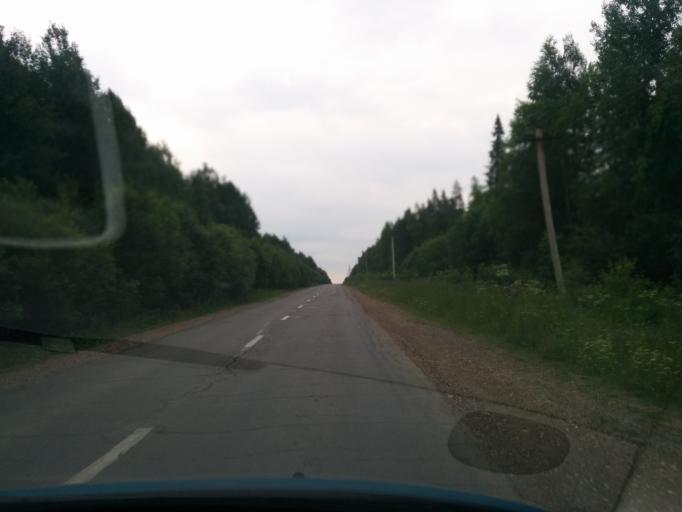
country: RU
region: Perm
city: Perm
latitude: 58.1966
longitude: 56.2147
